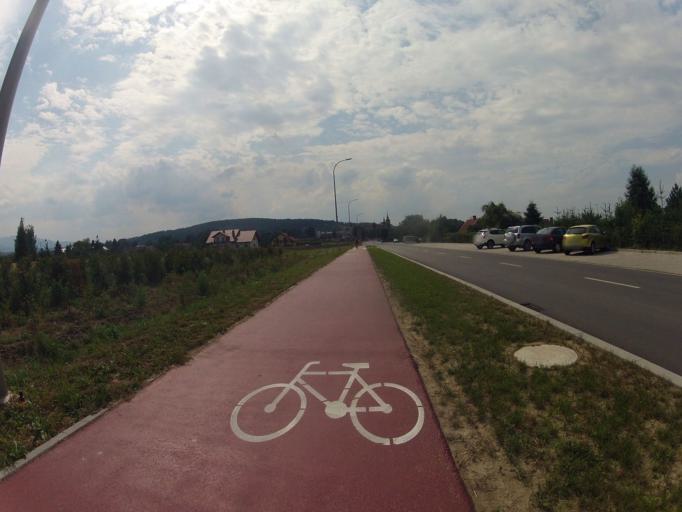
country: PL
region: Lesser Poland Voivodeship
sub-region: Powiat nowosadecki
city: Stary Sacz
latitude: 49.5617
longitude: 20.6480
